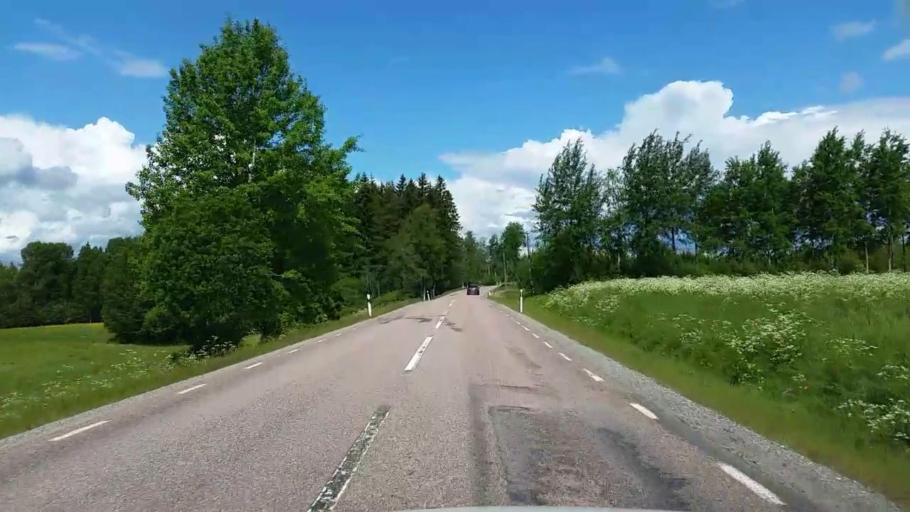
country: SE
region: Vaestmanland
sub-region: Fagersta Kommun
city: Fagersta
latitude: 59.9418
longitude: 15.8049
